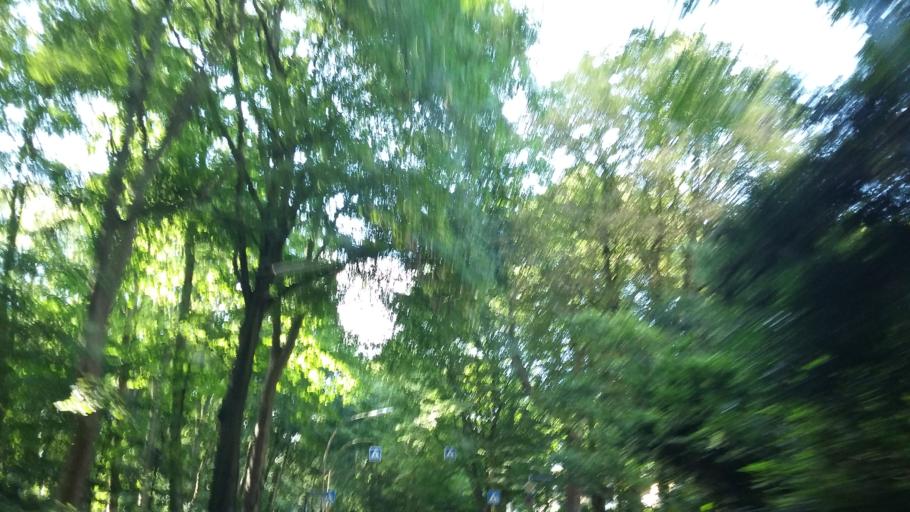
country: DE
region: Schleswig-Holstein
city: Halstenbek
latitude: 53.5572
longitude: 9.8312
